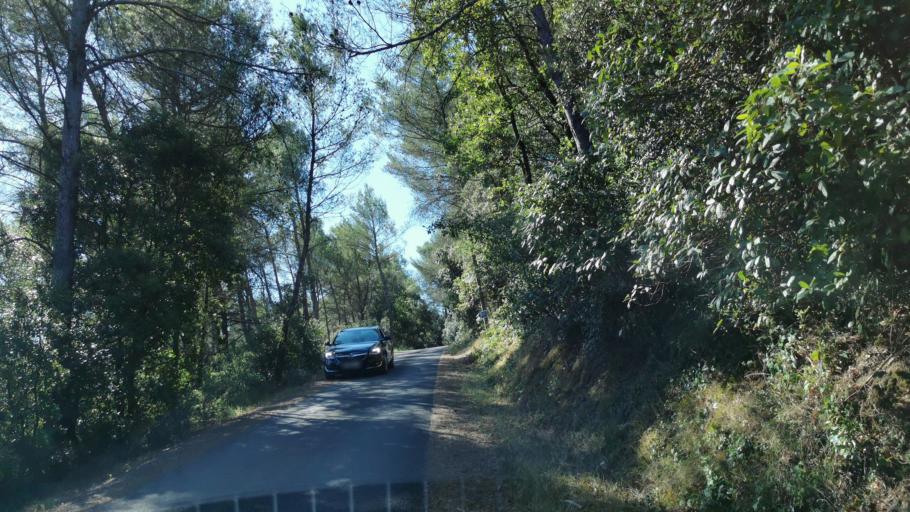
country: FR
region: Languedoc-Roussillon
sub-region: Departement de l'Aude
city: Conques-sur-Orbiel
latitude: 43.2460
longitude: 2.4109
